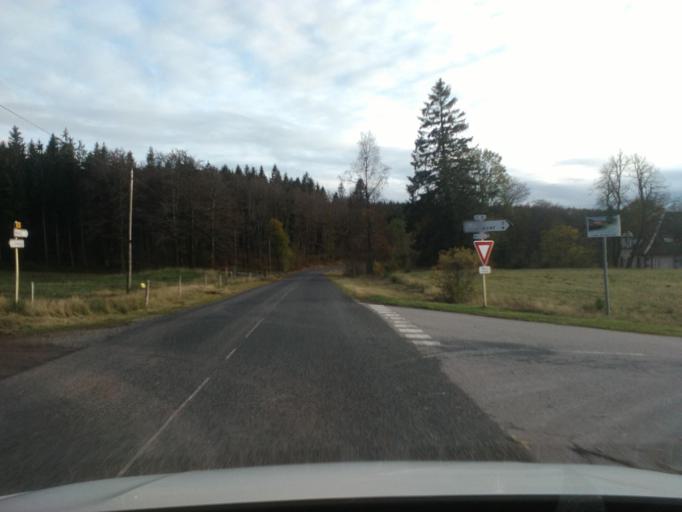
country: FR
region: Lorraine
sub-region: Departement des Vosges
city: Senones
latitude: 48.3826
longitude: 7.0970
